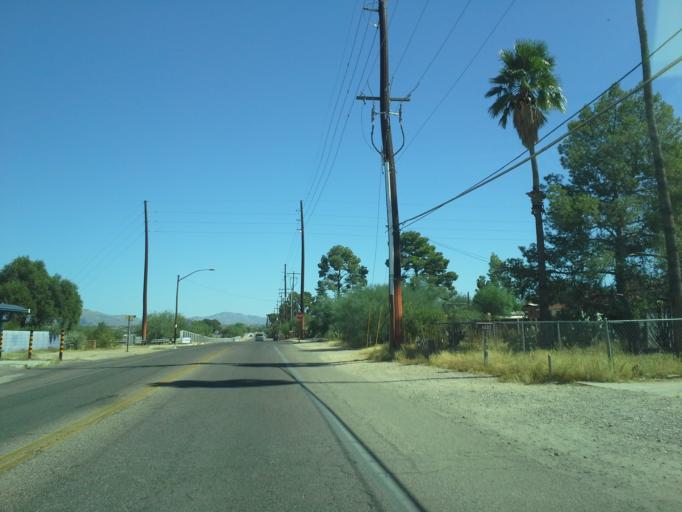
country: US
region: Arizona
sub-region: Pima County
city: Catalina Foothills
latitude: 32.2794
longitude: -110.9534
